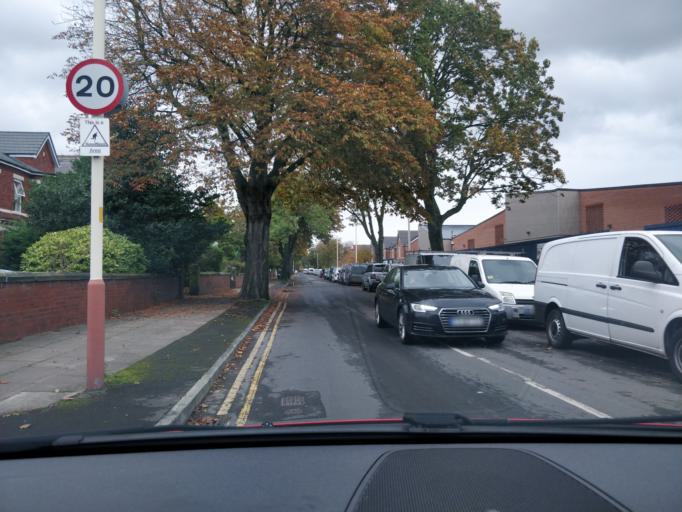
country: GB
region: England
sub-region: Sefton
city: Southport
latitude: 53.6384
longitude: -2.9877
